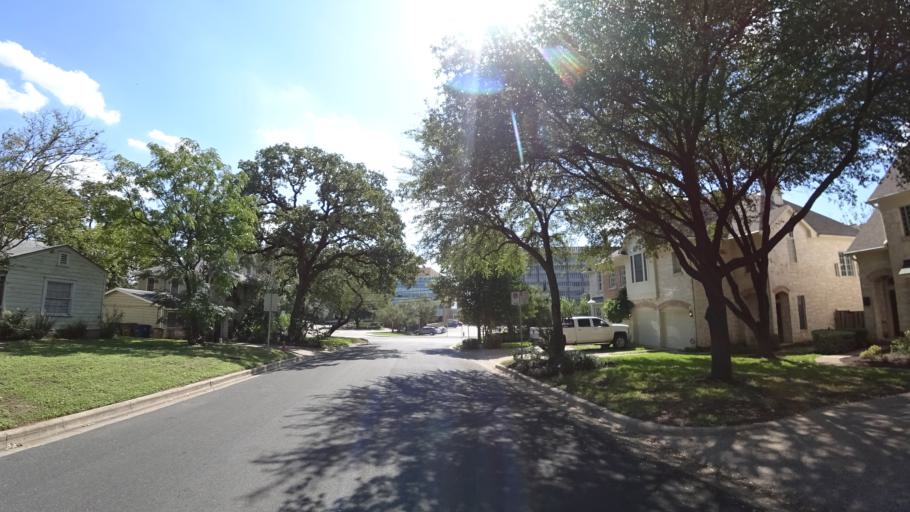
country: US
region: Texas
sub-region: Travis County
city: Austin
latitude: 30.3069
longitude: -97.7456
